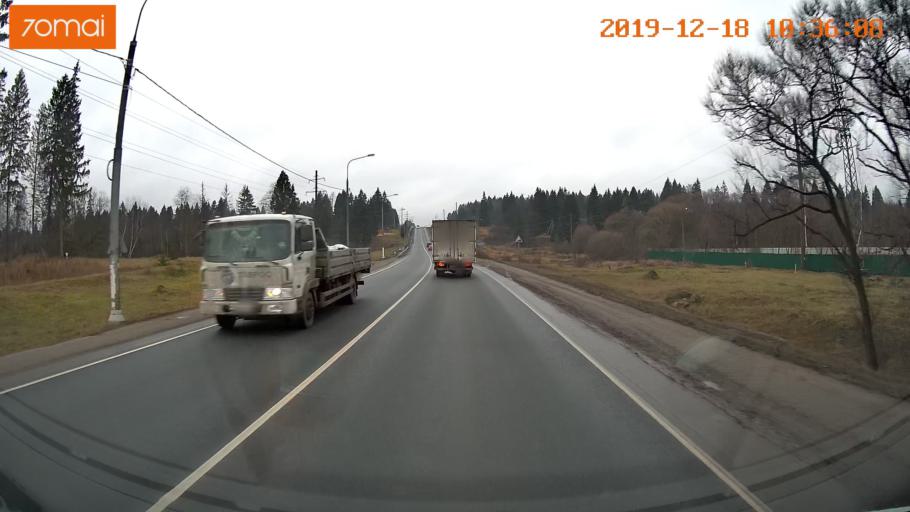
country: RU
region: Moskovskaya
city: Troitsk
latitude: 55.4183
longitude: 37.1894
